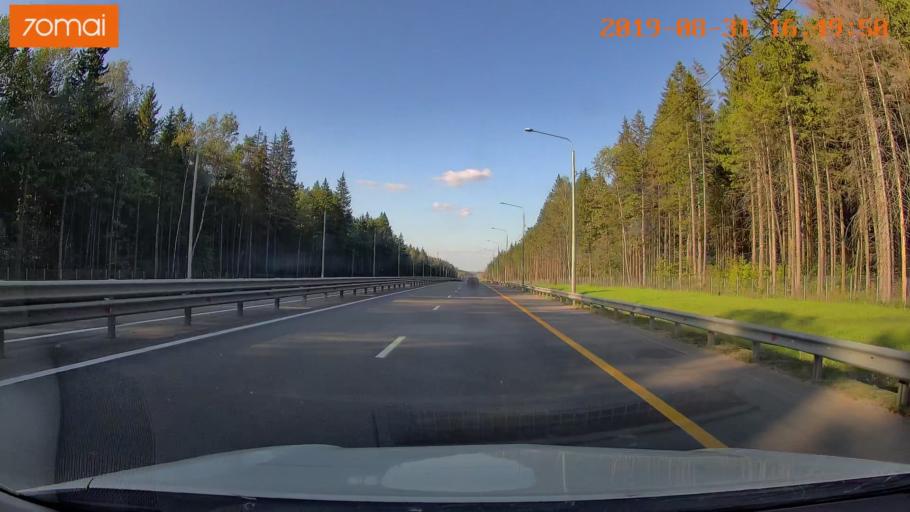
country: RU
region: Kaluga
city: Pyatovskiy
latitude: 54.6978
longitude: 36.1580
